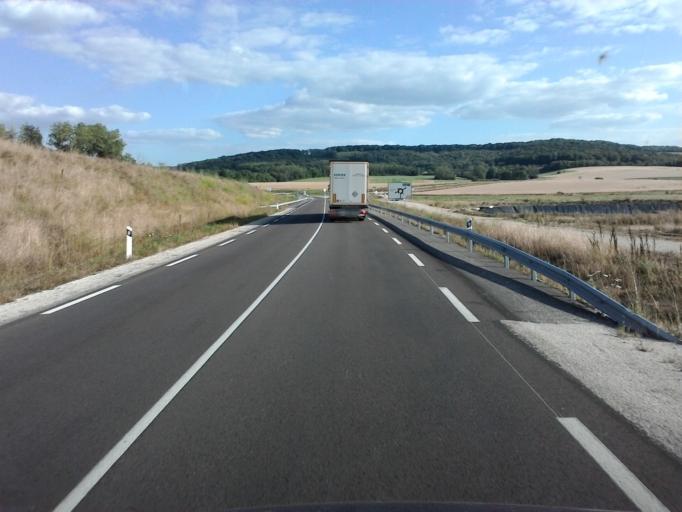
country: FR
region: Franche-Comte
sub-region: Departement de la Haute-Saone
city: Frotey-les-Vesoul
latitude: 47.6895
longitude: 6.2661
